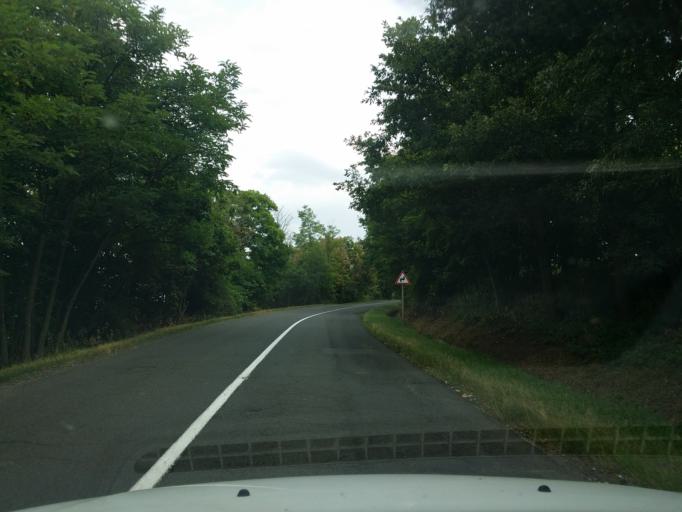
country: HU
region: Nograd
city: Bercel
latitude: 47.9399
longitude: 19.3726
